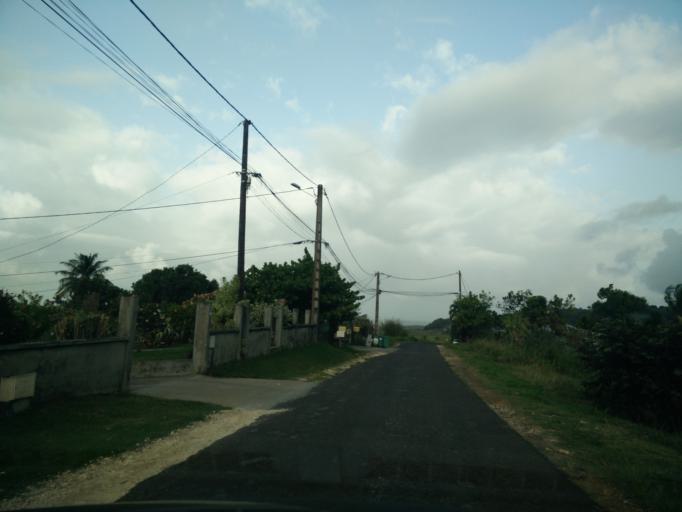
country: GP
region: Guadeloupe
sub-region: Guadeloupe
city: Petit-Bourg
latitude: 16.1841
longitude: -61.6108
